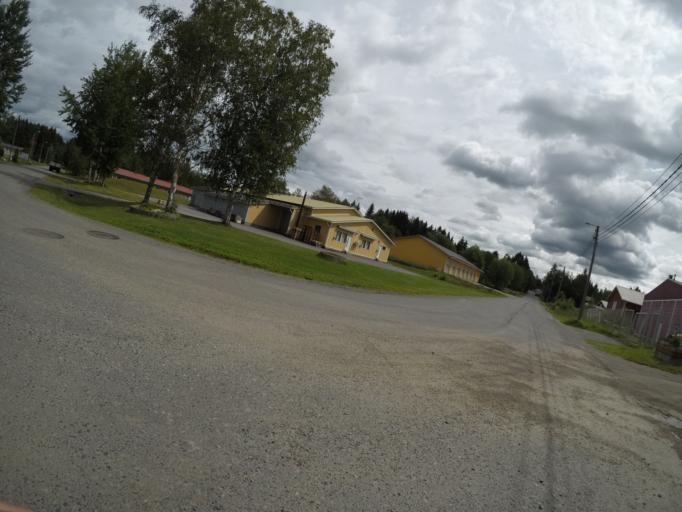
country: FI
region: Haeme
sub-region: Haemeenlinna
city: Haemeenlinna
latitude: 60.9666
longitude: 24.4355
